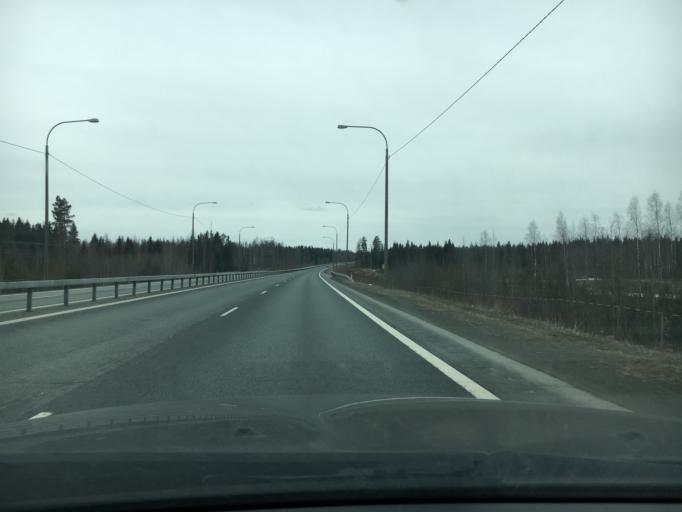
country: FI
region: Northern Savo
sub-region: Kuopio
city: Kuopio
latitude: 62.7476
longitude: 27.5828
